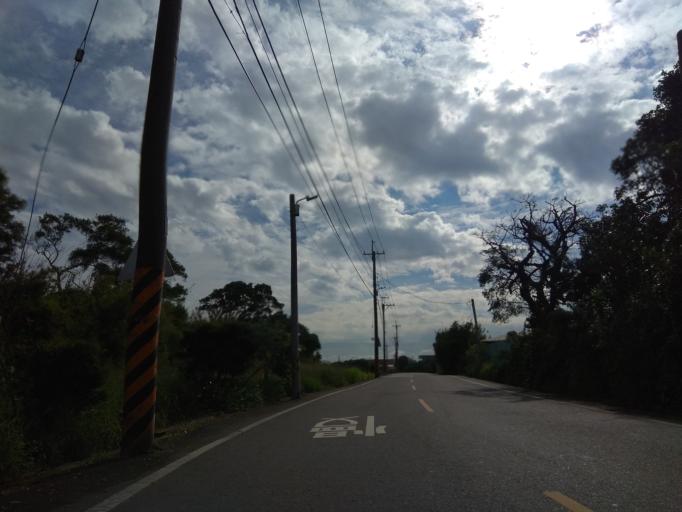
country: TW
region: Taiwan
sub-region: Hsinchu
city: Zhubei
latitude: 24.9587
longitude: 121.1073
